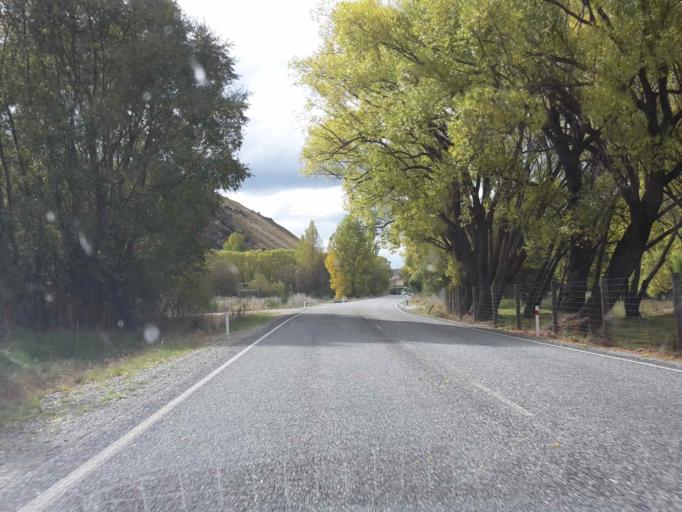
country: NZ
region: Otago
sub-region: Queenstown-Lakes District
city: Wanaka
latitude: -44.8350
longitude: 169.0560
